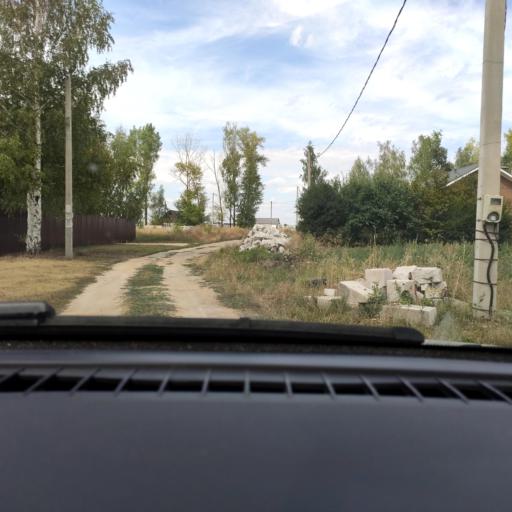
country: RU
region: Voronezj
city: Novaya Usman'
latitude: 51.6677
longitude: 39.4389
